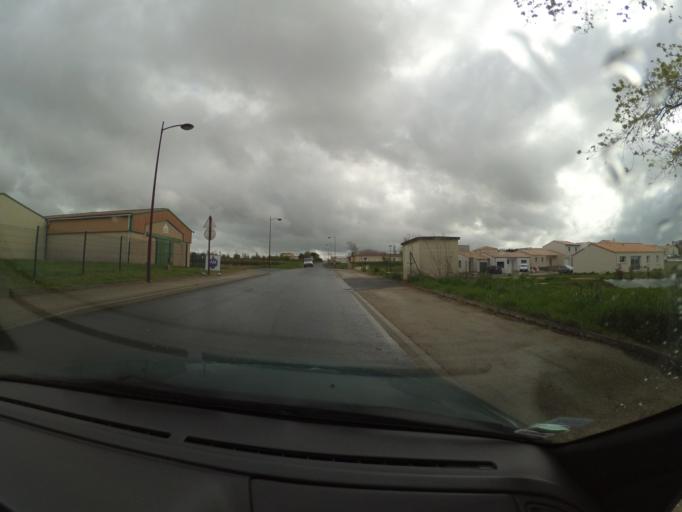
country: FR
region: Pays de la Loire
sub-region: Departement de la Loire-Atlantique
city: Monnieres
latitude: 47.1330
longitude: -1.3511
